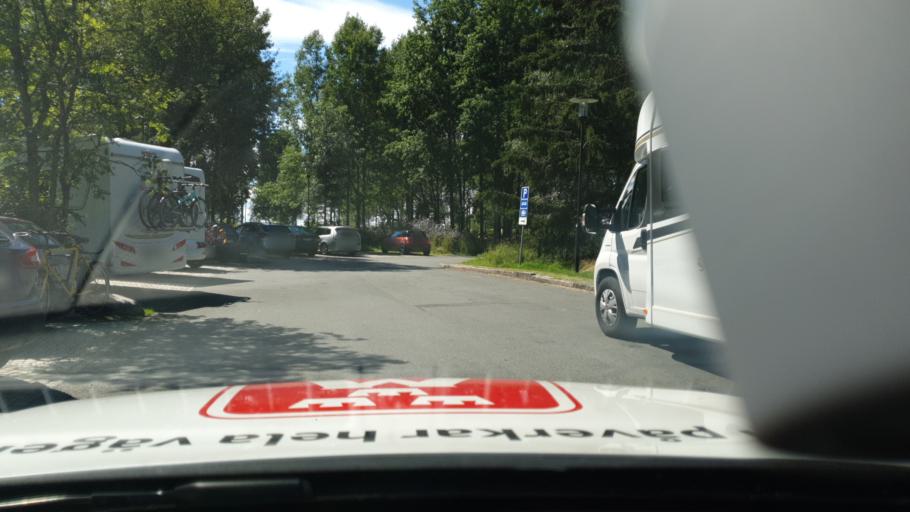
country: SE
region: Joenkoeping
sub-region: Nassjo Kommun
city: Nassjo
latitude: 57.6805
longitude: 14.6711
